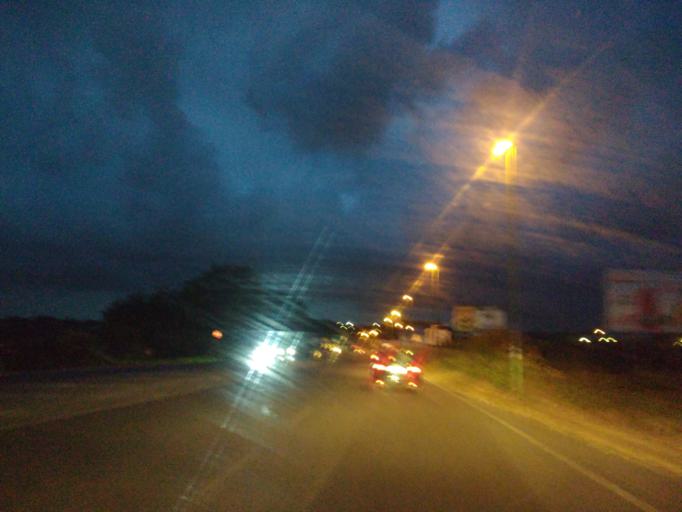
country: IT
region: Latium
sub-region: Citta metropolitana di Roma Capitale
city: Anzio
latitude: 41.4606
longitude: 12.6215
